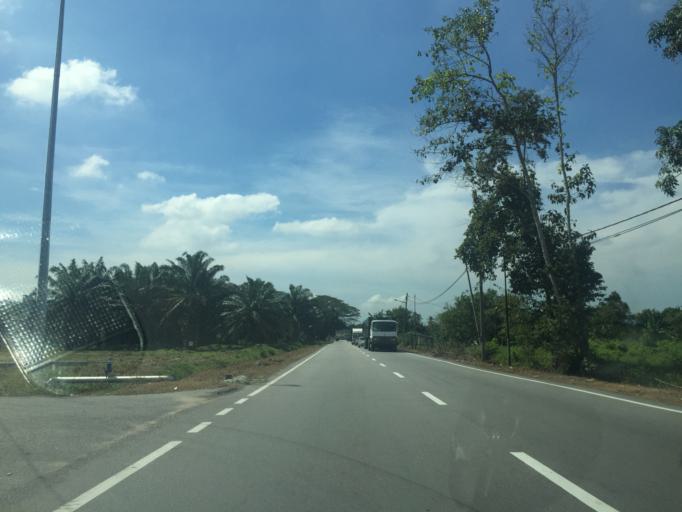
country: MY
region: Penang
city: Tasek Glugor
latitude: 5.4896
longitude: 100.5057
